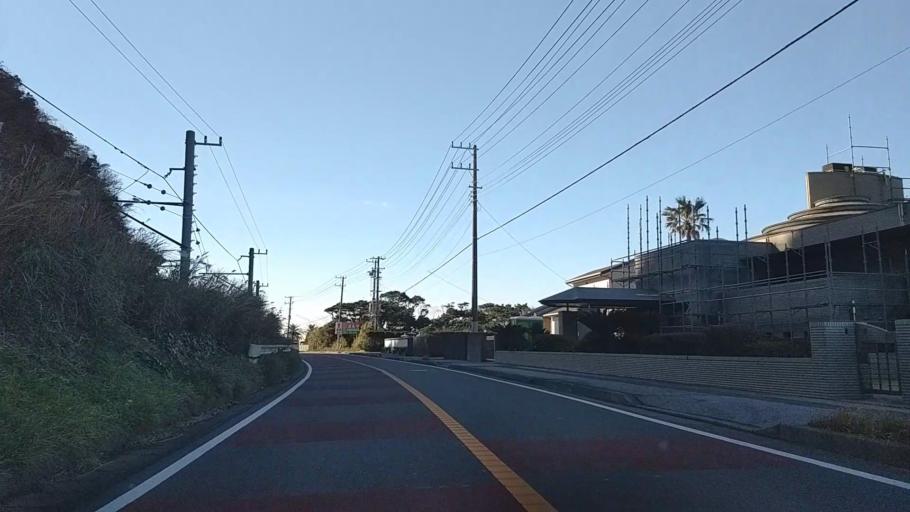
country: JP
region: Chiba
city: Futtsu
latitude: 35.1903
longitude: 139.8204
